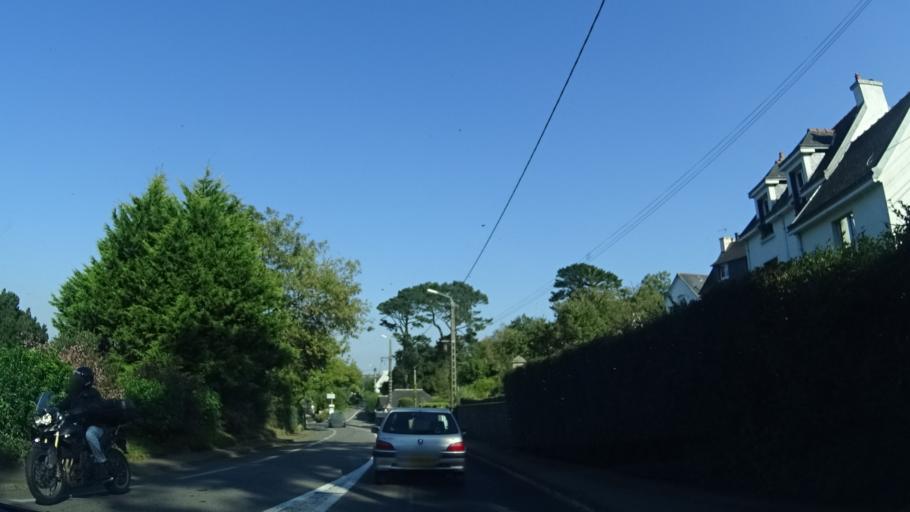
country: FR
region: Brittany
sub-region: Departement du Finistere
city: Douarnenez
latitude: 48.0878
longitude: -4.3058
